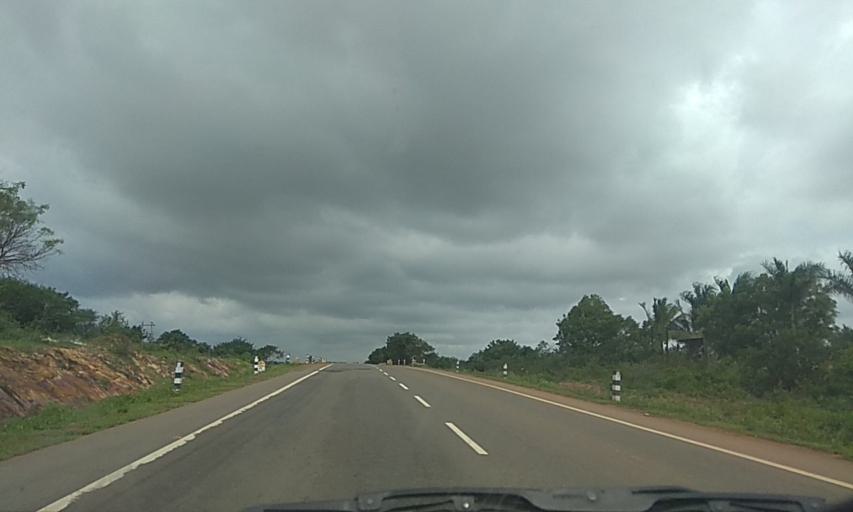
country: IN
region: Karnataka
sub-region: Dharwad
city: Hubli
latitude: 15.3419
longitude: 75.0809
